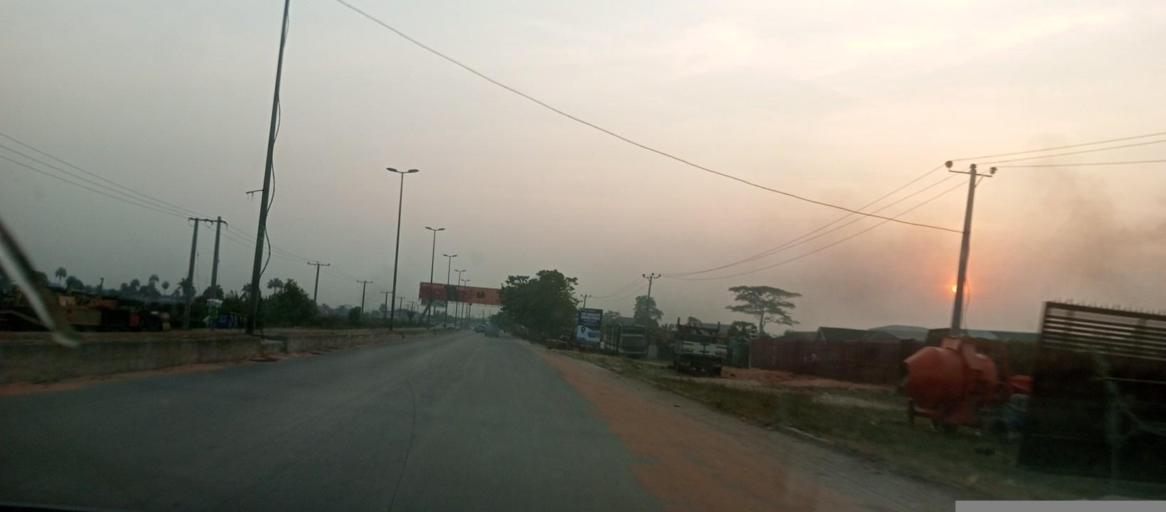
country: NG
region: Rivers
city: Emuoha
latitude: 4.9304
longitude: 7.0017
